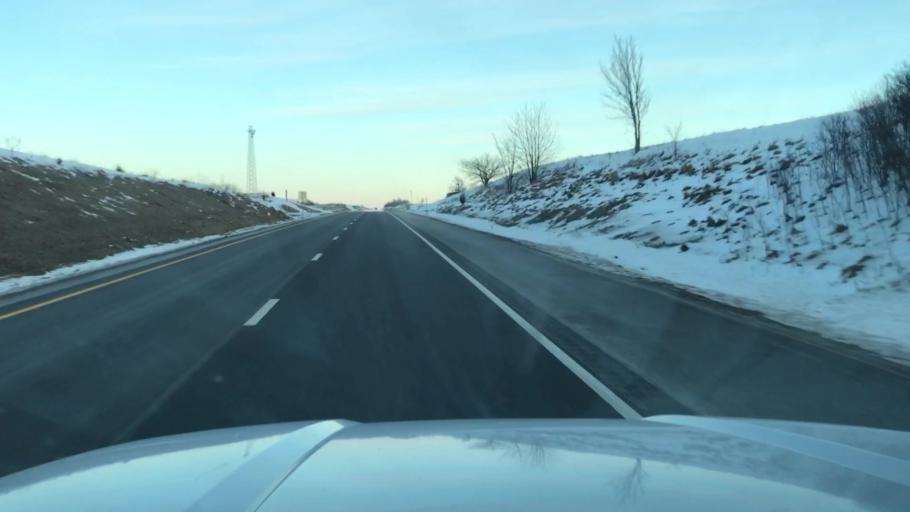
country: US
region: Missouri
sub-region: Clinton County
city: Gower
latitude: 39.7616
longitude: -94.5437
